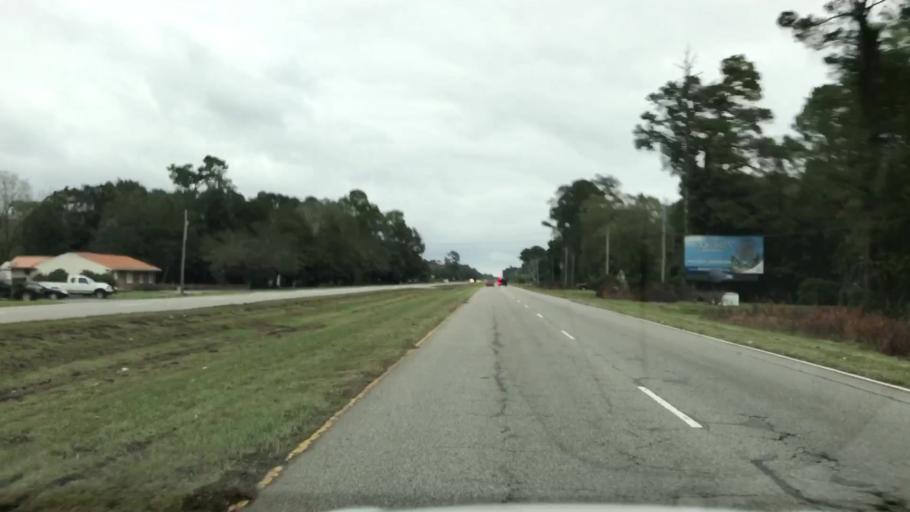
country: US
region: South Carolina
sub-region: Georgetown County
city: Georgetown
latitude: 33.3124
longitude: -79.3298
